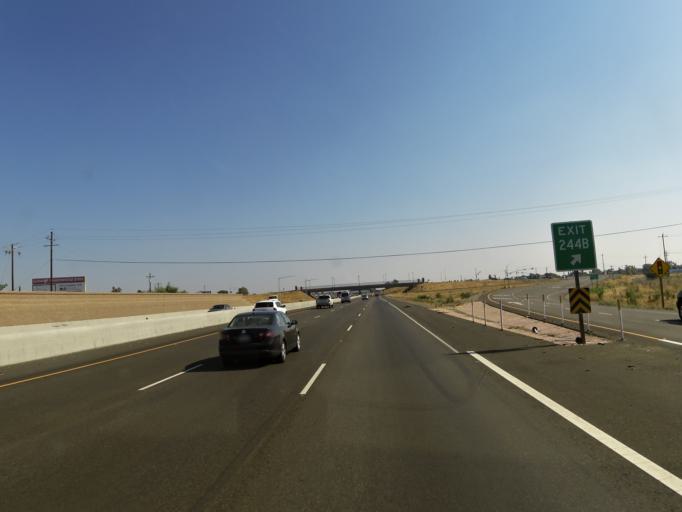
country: US
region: California
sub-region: San Joaquin County
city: Manteca
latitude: 37.8303
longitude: -121.2176
